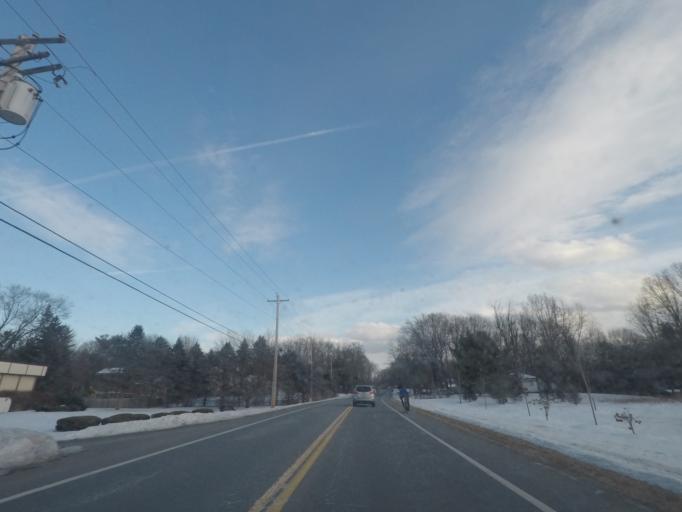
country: US
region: New York
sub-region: Saratoga County
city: Country Knolls
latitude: 42.8399
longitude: -73.7828
